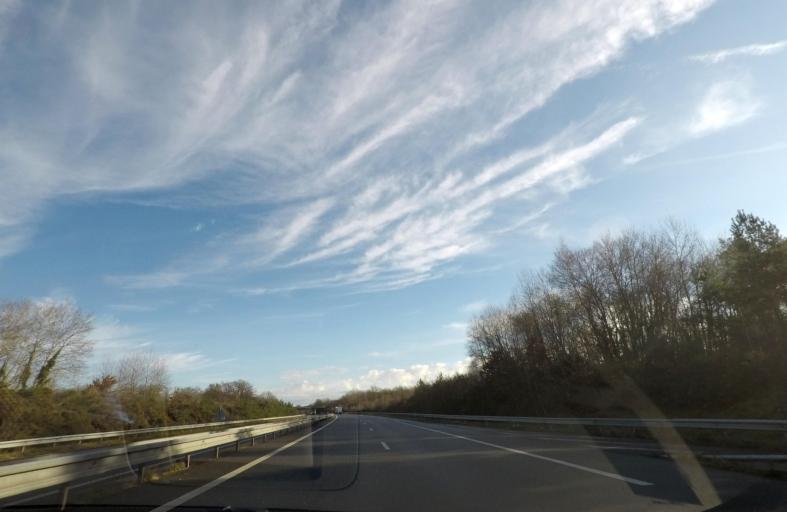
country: FR
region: Centre
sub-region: Departement du Loir-et-Cher
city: Theillay
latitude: 47.2899
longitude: 2.0194
